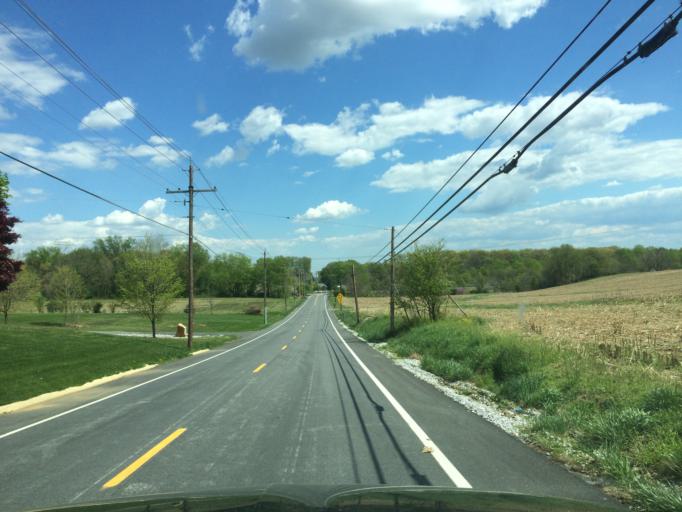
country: US
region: Maryland
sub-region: Carroll County
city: Eldersburg
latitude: 39.4311
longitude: -77.0111
